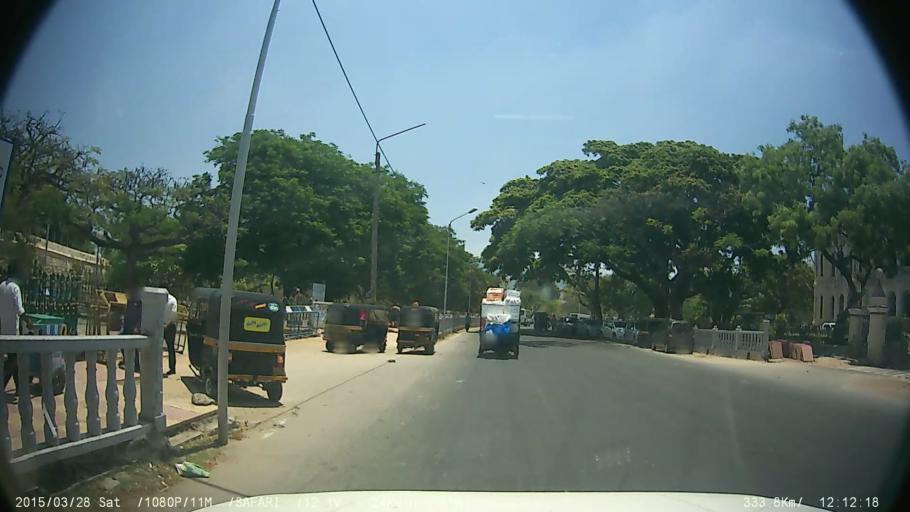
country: IN
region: Karnataka
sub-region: Mysore
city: Mysore
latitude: 12.3041
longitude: 76.6524
